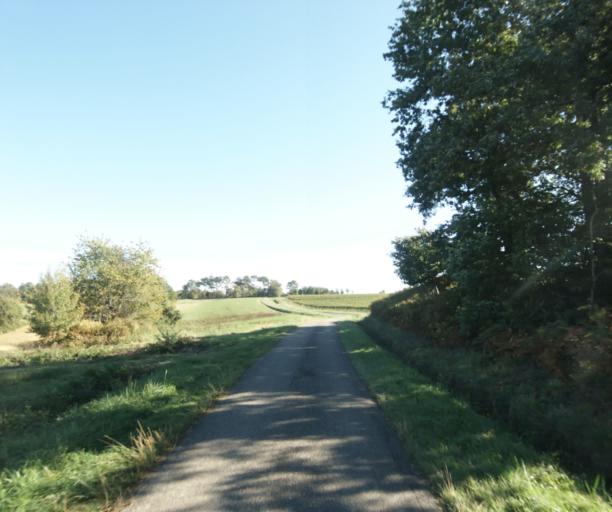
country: FR
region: Midi-Pyrenees
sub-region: Departement du Gers
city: Cazaubon
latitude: 43.8458
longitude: -0.0801
